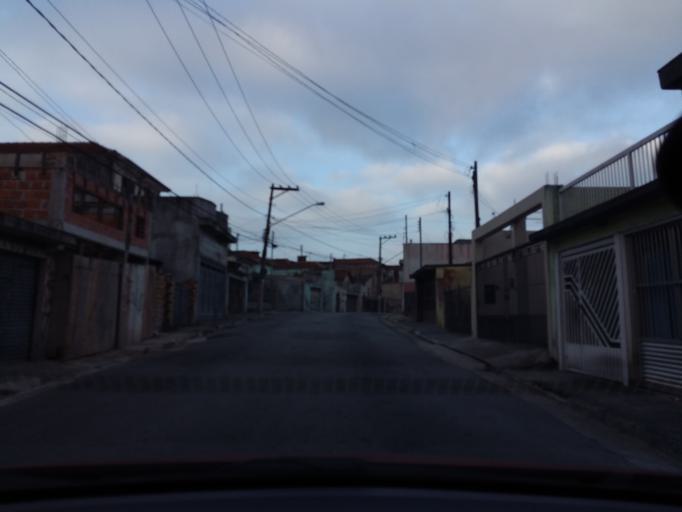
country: BR
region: Sao Paulo
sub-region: Sao Caetano Do Sul
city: Sao Caetano do Sul
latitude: -23.6322
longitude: -46.5860
